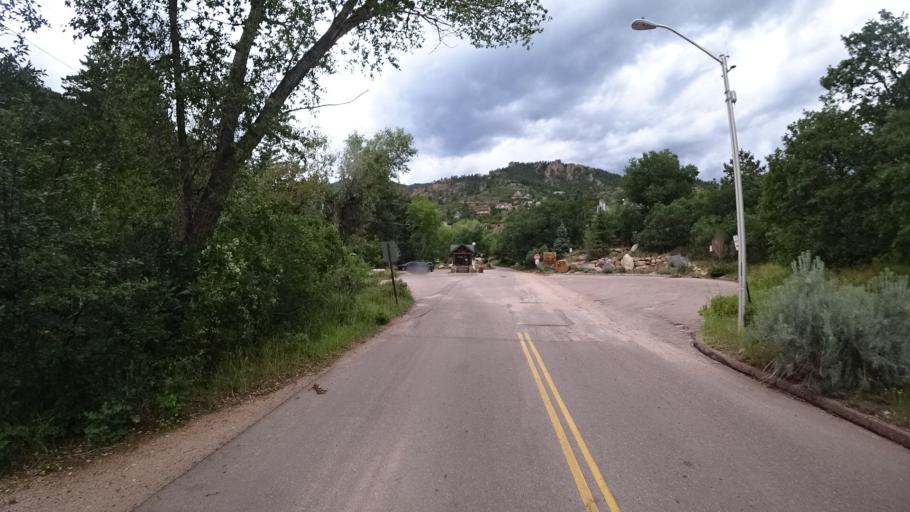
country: US
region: Colorado
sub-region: El Paso County
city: Manitou Springs
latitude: 38.8425
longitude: -104.9038
